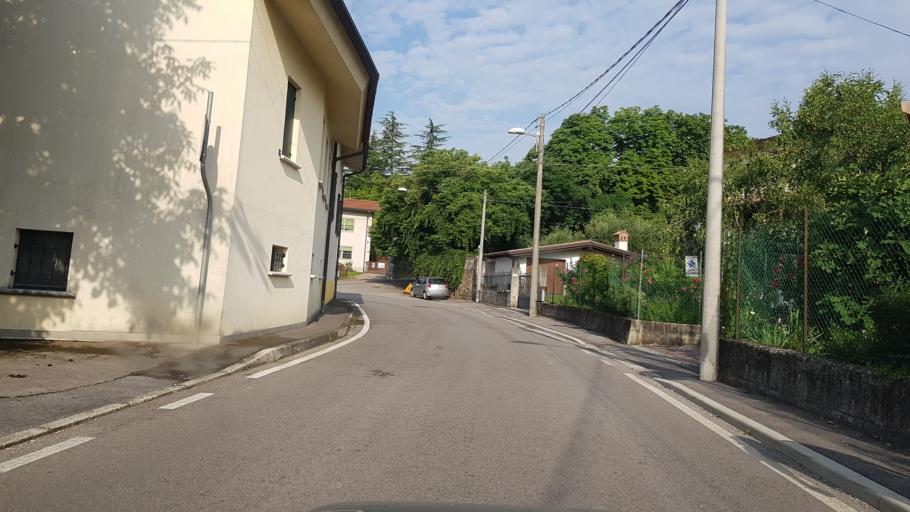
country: IT
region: Friuli Venezia Giulia
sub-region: Provincia di Gorizia
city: Mossa
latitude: 45.9381
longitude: 13.5435
